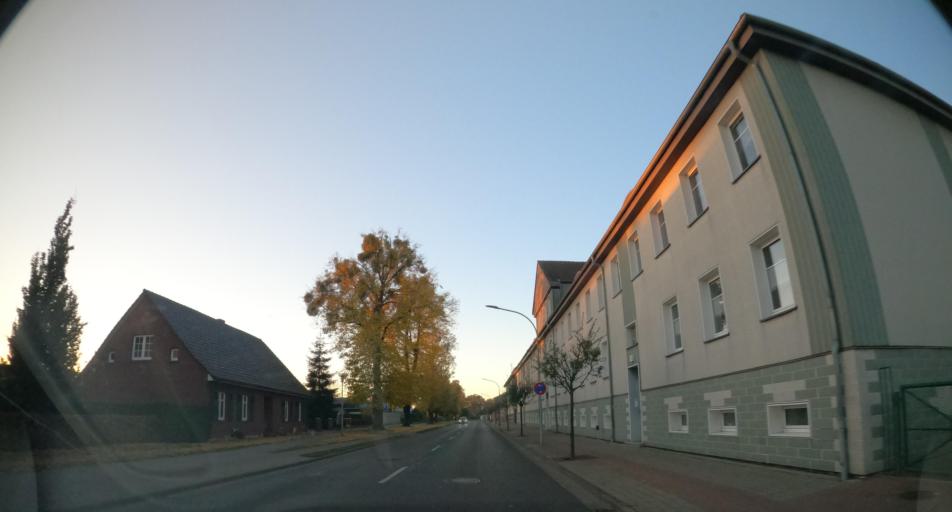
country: DE
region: Mecklenburg-Vorpommern
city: Ueckermunde
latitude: 53.7404
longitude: 14.0375
